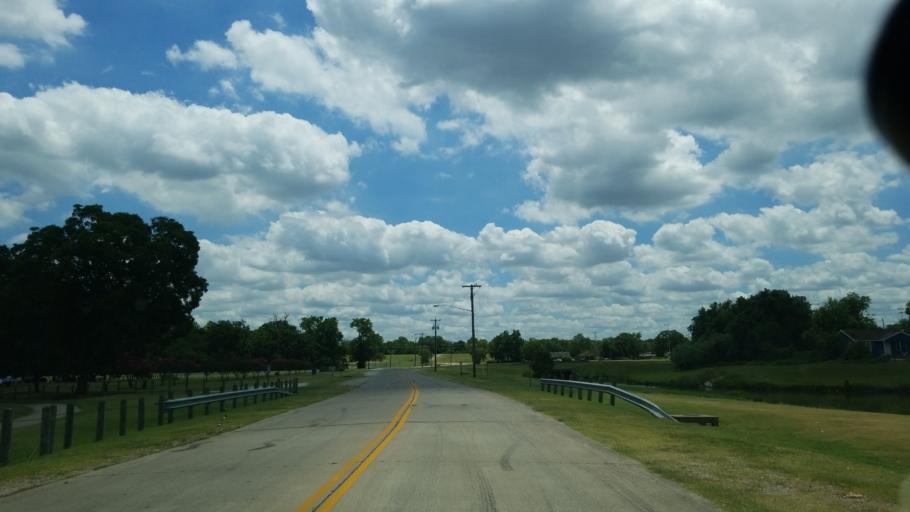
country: US
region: Texas
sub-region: Dallas County
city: Dallas
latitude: 32.7437
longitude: -96.7455
